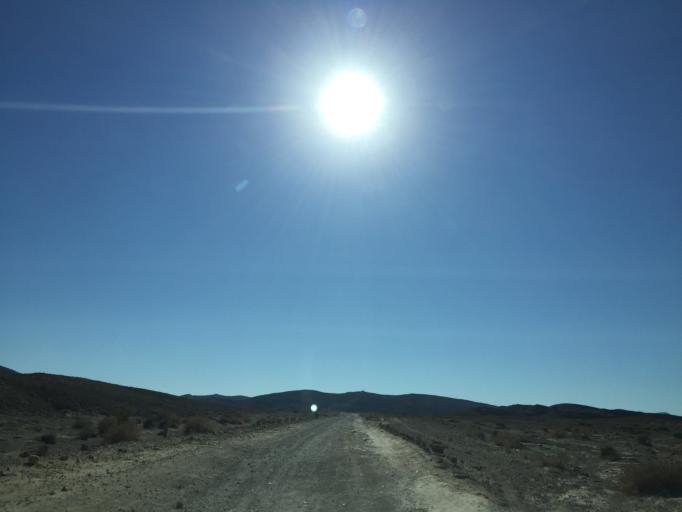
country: IL
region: Southern District
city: Mitzpe Ramon
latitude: 30.6079
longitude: 34.8993
